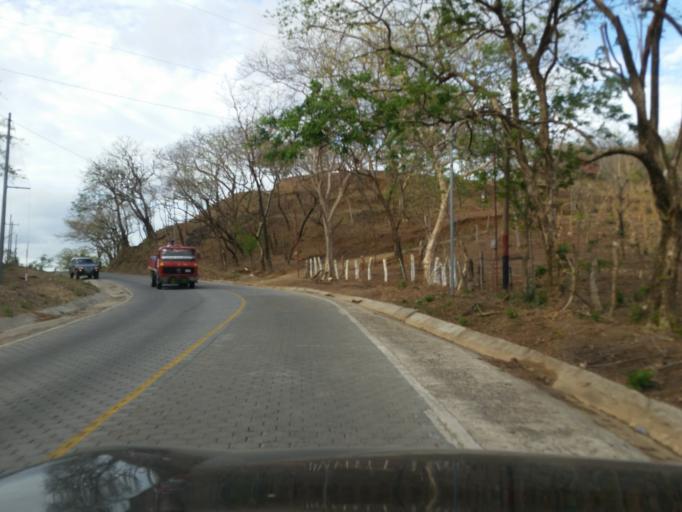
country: NI
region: Rivas
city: Tola
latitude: 11.4100
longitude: -85.9542
